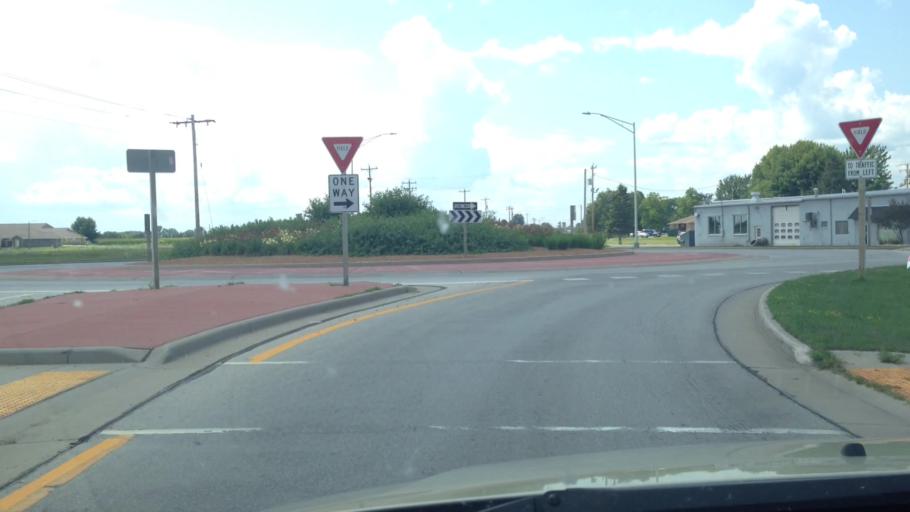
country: US
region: Wisconsin
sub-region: Brown County
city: Pulaski
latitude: 44.6572
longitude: -88.2212
